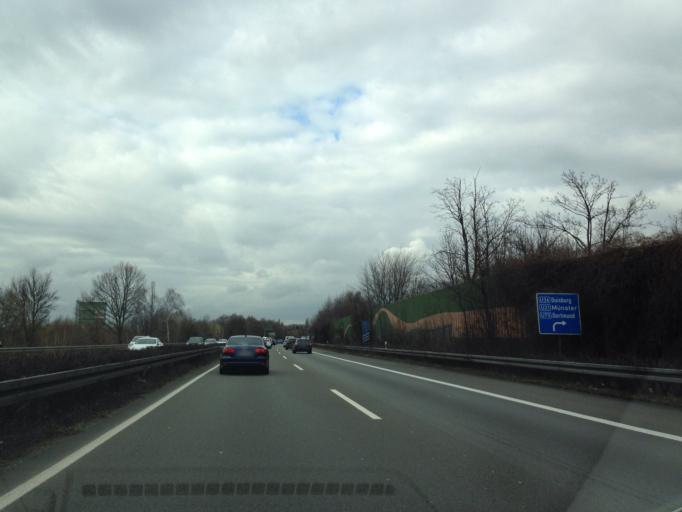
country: DE
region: North Rhine-Westphalia
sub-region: Regierungsbezirk Arnsberg
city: Herne
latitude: 51.5241
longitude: 7.2088
